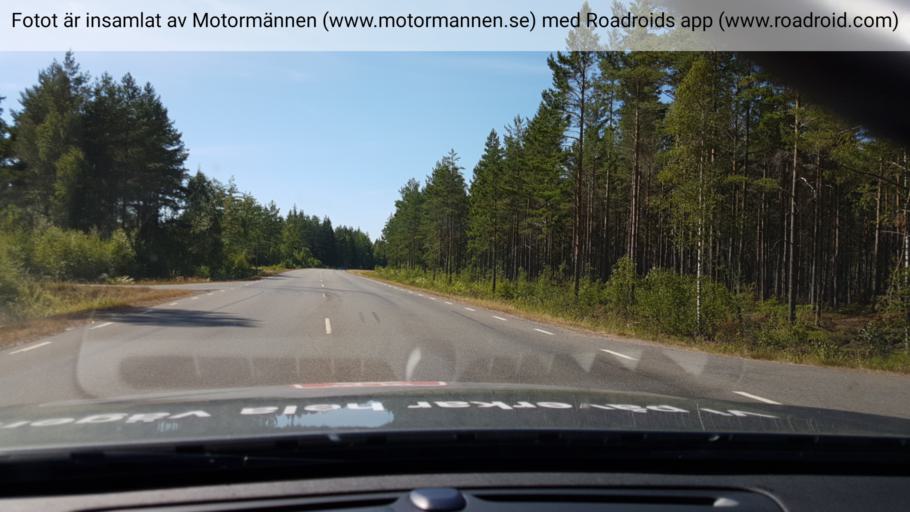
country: SE
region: Vaestra Goetaland
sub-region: Karlsborgs Kommun
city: Karlsborg
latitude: 58.5780
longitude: 14.4596
